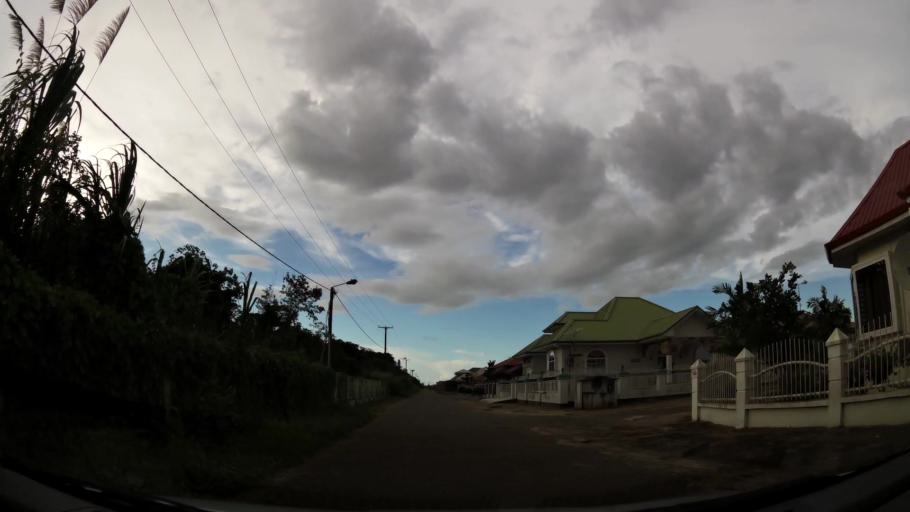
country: SR
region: Paramaribo
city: Paramaribo
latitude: 5.8622
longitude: -55.1769
